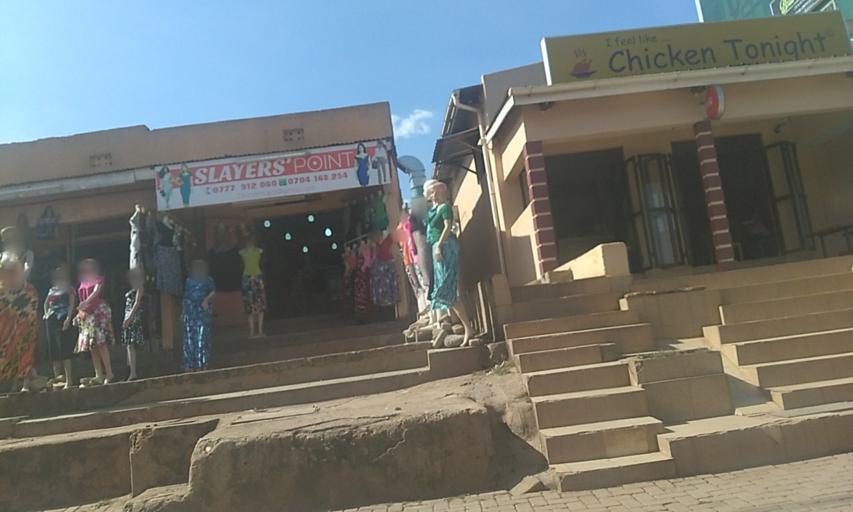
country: UG
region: Central Region
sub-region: Wakiso District
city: Kireka
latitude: 0.3542
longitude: 32.6117
